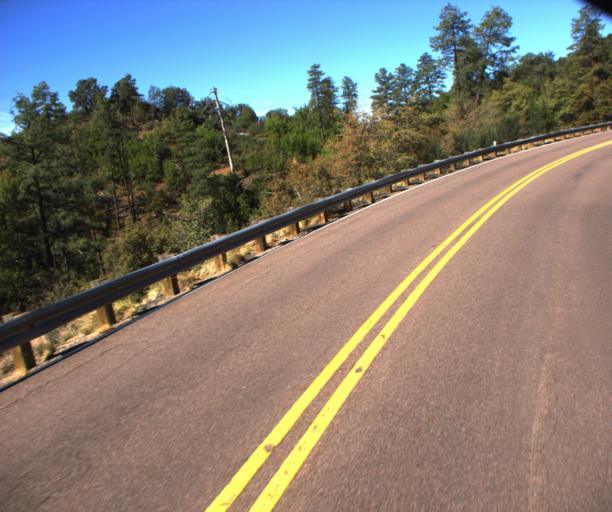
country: US
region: Arizona
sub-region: Yavapai County
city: Prescott
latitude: 34.4808
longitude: -112.5031
